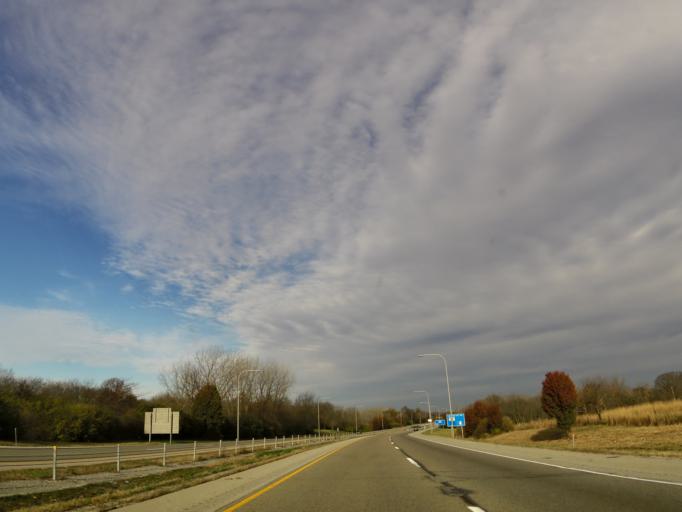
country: US
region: Illinois
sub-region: Champaign County
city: Urbana
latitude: 40.1230
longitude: -88.1769
